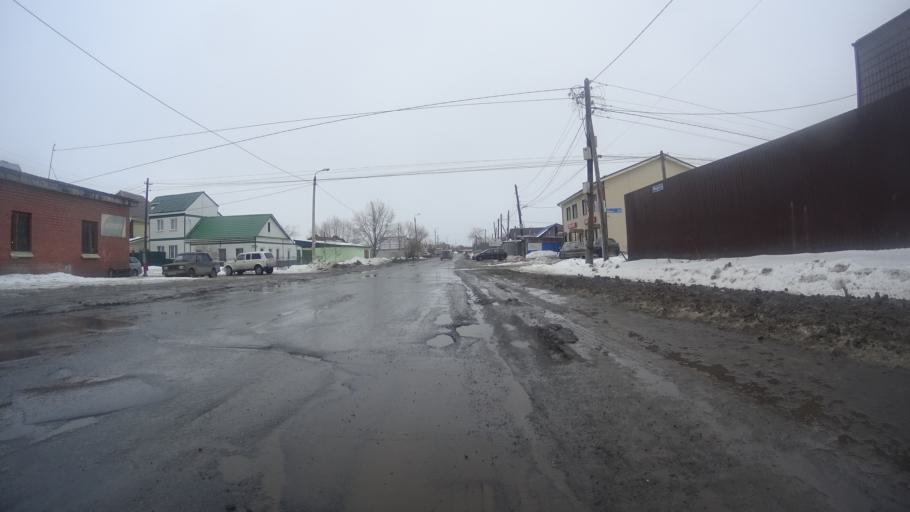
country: RU
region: Chelyabinsk
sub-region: Gorod Chelyabinsk
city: Chelyabinsk
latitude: 55.1299
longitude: 61.3894
